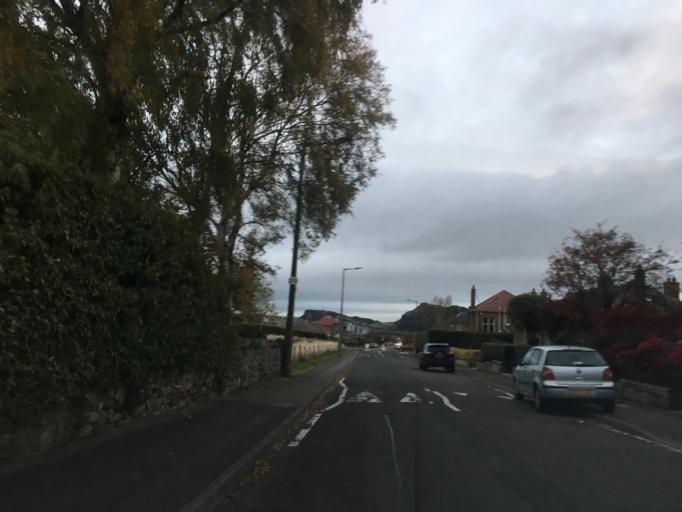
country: GB
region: Scotland
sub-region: Midlothian
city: Loanhead
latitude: 55.9107
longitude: -3.1686
